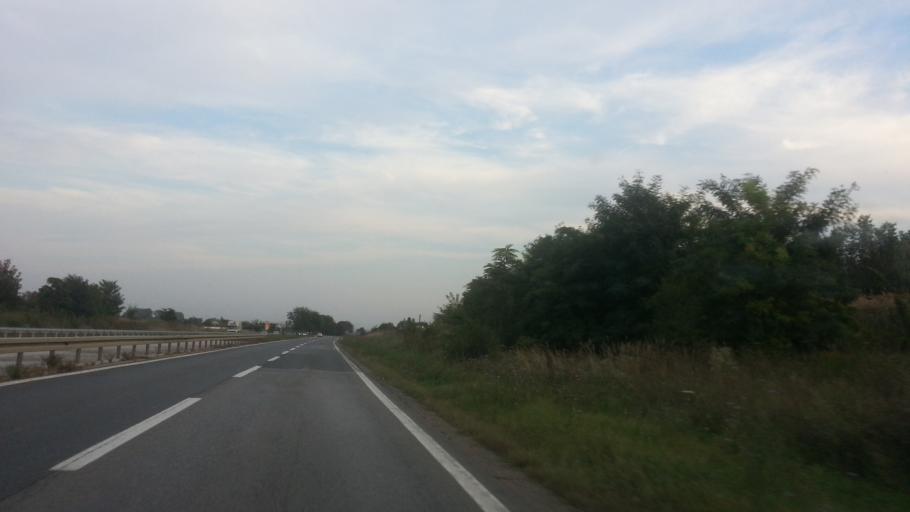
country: RS
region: Central Serbia
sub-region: Belgrade
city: Zemun
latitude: 44.8767
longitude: 20.3267
